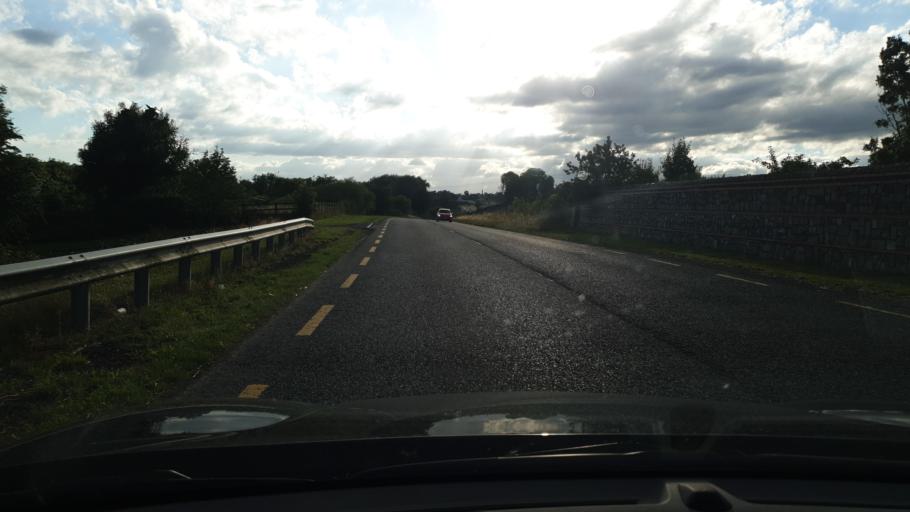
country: IE
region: Leinster
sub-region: An Mhi
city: Stamullin
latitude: 53.6721
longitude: -6.2993
